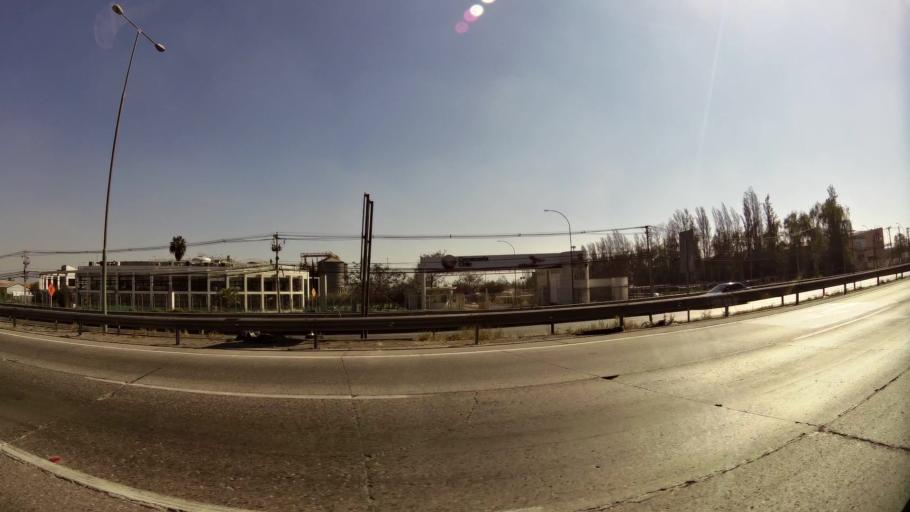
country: CL
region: Santiago Metropolitan
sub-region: Provincia de Chacabuco
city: Chicureo Abajo
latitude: -33.3364
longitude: -70.7135
